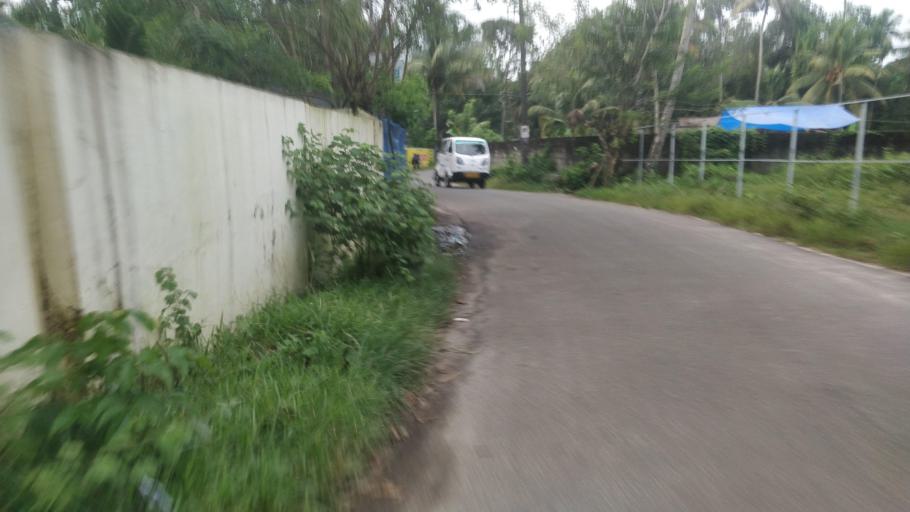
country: IN
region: Kerala
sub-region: Alappuzha
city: Vayalar
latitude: 9.7029
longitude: 76.3482
